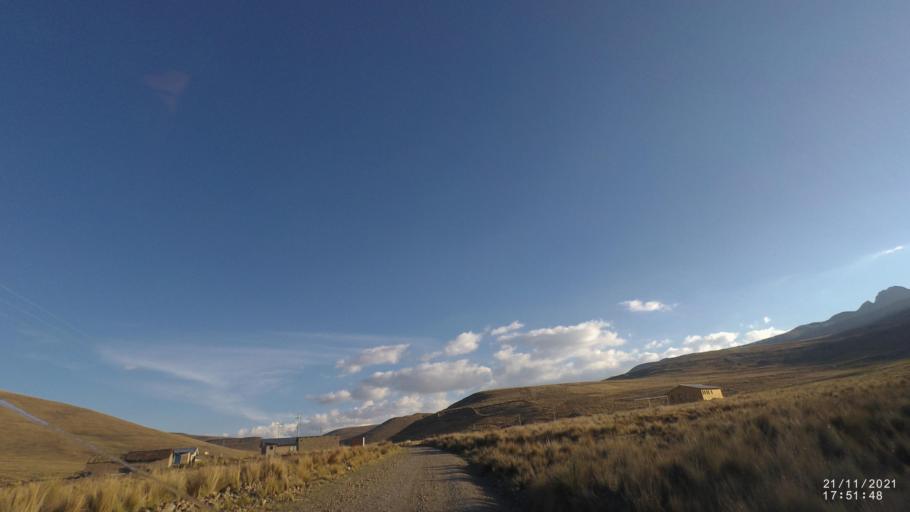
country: BO
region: Cochabamba
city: Cochabamba
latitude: -17.2050
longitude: -66.2427
